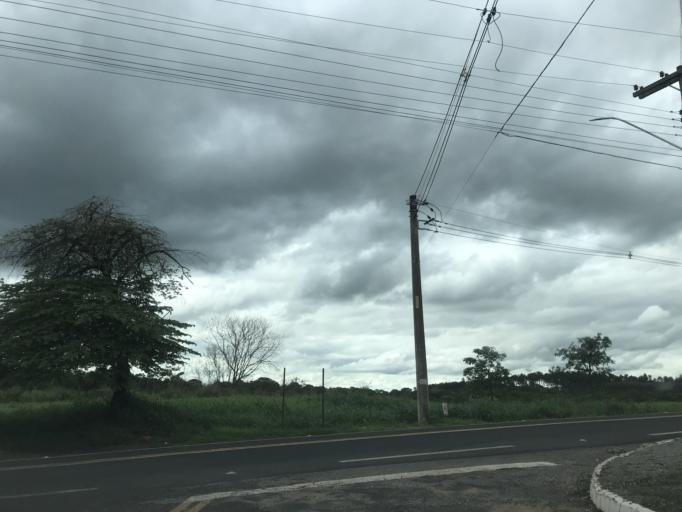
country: BR
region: Goias
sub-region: Caldas Novas
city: Caldas Novas
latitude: -17.7677
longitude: -48.7594
